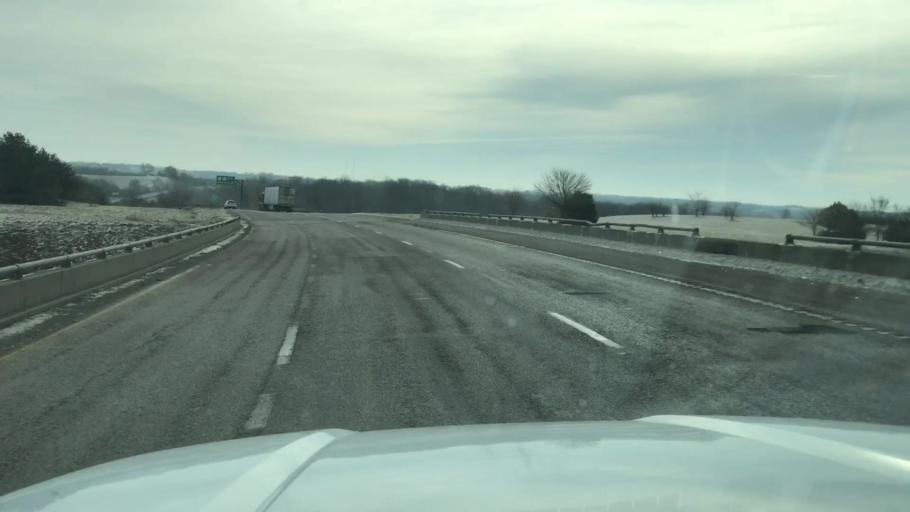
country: US
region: Missouri
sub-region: Andrew County
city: Country Club Village
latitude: 39.8845
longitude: -94.8565
